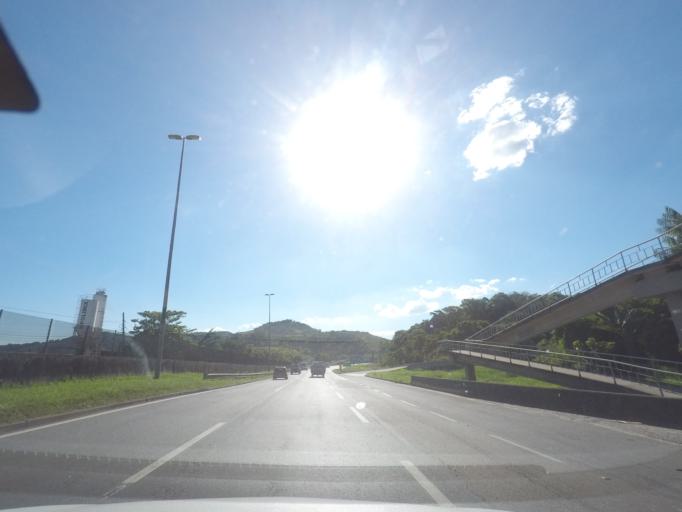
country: BR
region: Rio de Janeiro
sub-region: Petropolis
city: Petropolis
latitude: -22.6567
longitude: -43.1276
